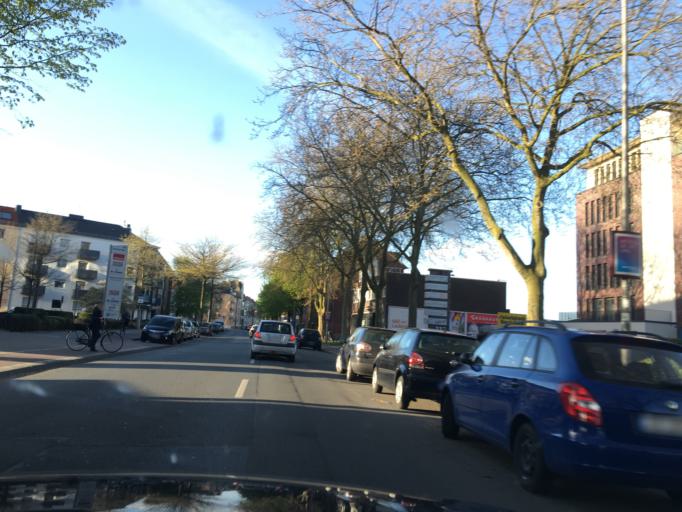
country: DE
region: North Rhine-Westphalia
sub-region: Regierungsbezirk Munster
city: Muenster
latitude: 51.9465
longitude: 7.6310
